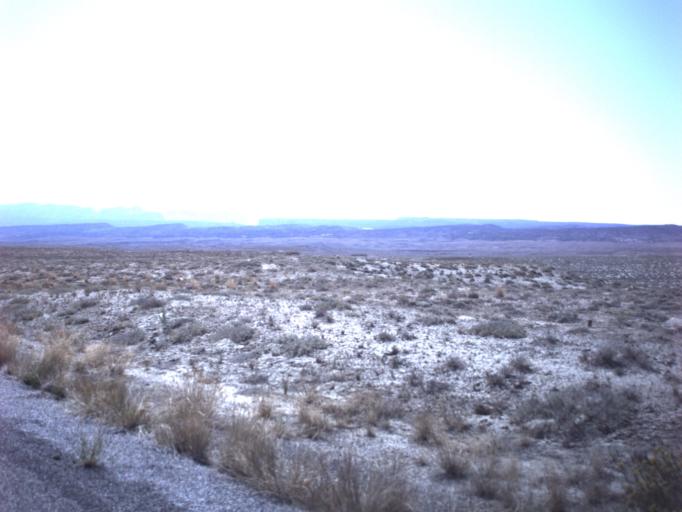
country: US
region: Utah
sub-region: Grand County
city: Moab
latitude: 38.9246
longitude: -109.3381
